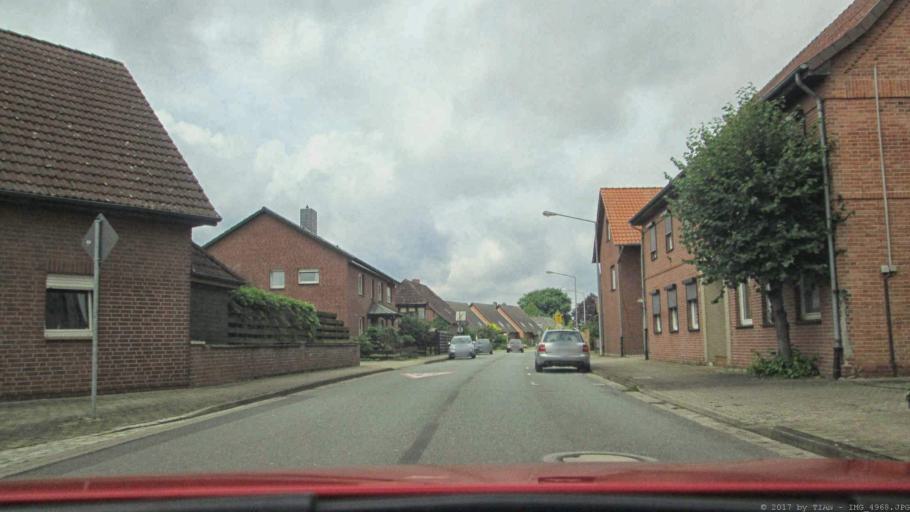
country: DE
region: Lower Saxony
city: Tappenbeck
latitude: 52.4568
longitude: 10.7482
